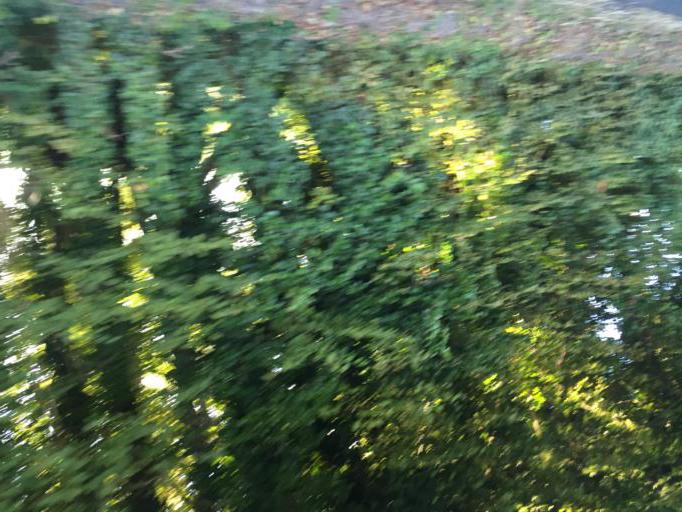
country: FR
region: Lower Normandy
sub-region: Departement du Calvados
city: Equemauville
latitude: 49.4069
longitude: 0.1768
